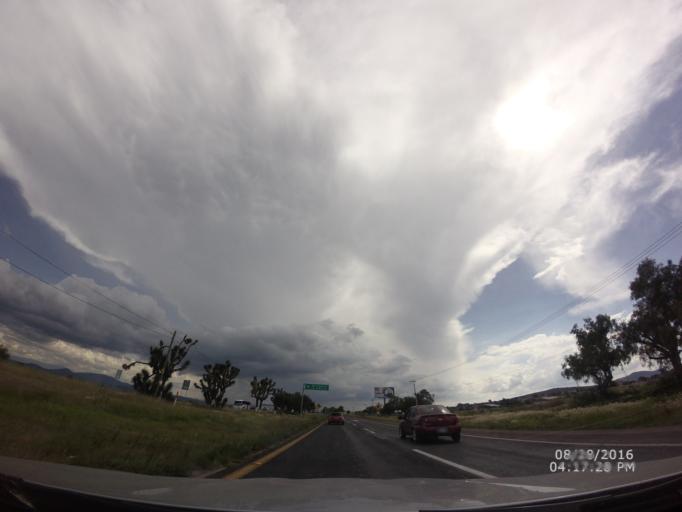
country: MX
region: Hidalgo
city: Zapotlan de Juarez
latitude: 19.9756
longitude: -98.8513
